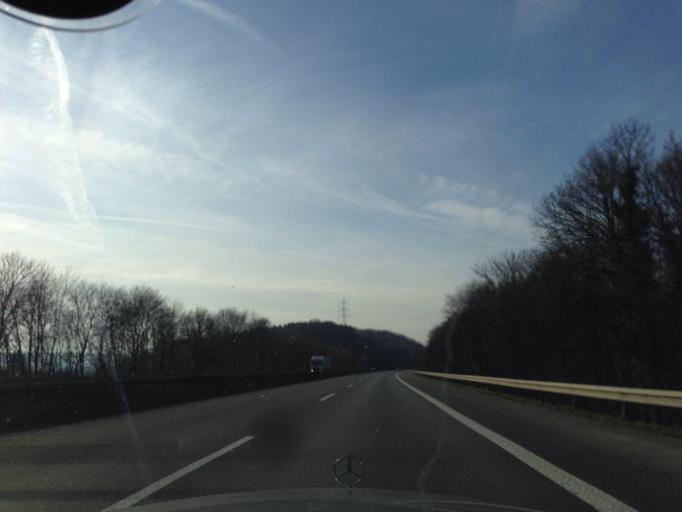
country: DE
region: North Rhine-Westphalia
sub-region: Regierungsbezirk Munster
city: Tecklenburg
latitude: 52.2541
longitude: 7.8140
